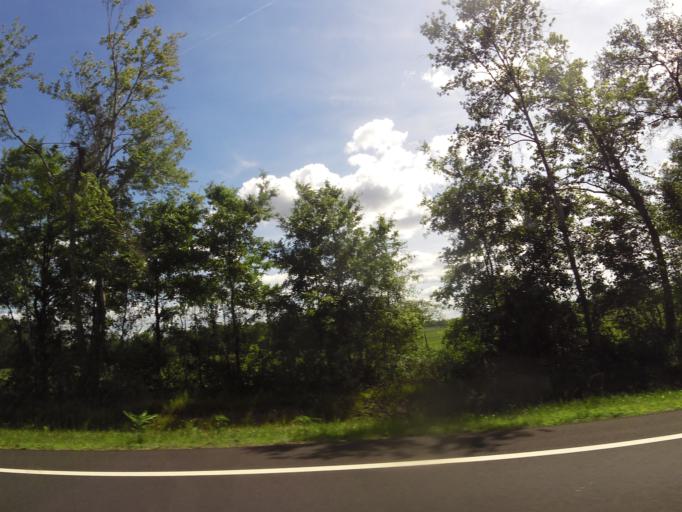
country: US
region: Florida
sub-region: Nassau County
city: Callahan
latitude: 30.6071
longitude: -81.8723
